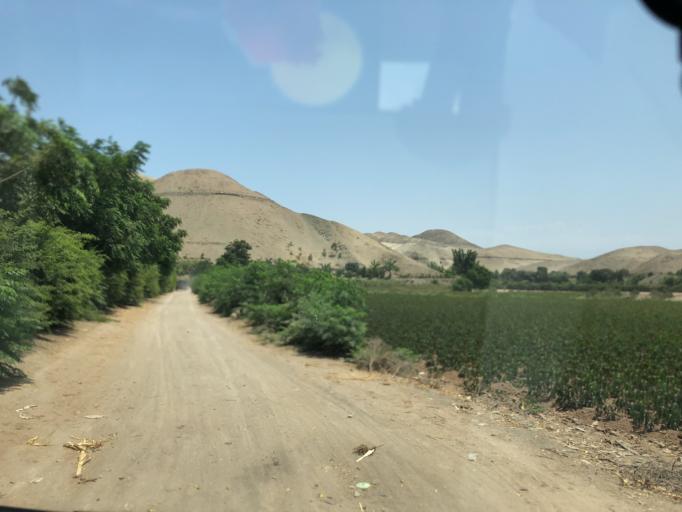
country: PE
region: Lima
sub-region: Provincia de Canete
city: Quilmana
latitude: -12.9989
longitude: -76.4462
